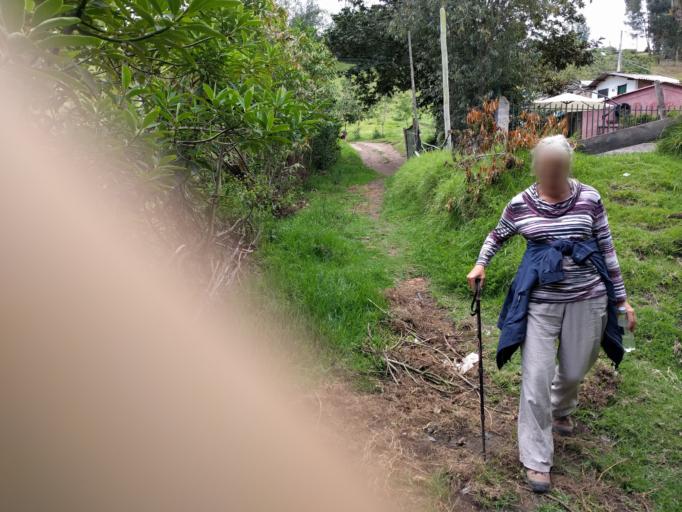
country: EC
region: Imbabura
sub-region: Canton Otavalo
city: Otavalo
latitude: 0.2133
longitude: -78.2697
